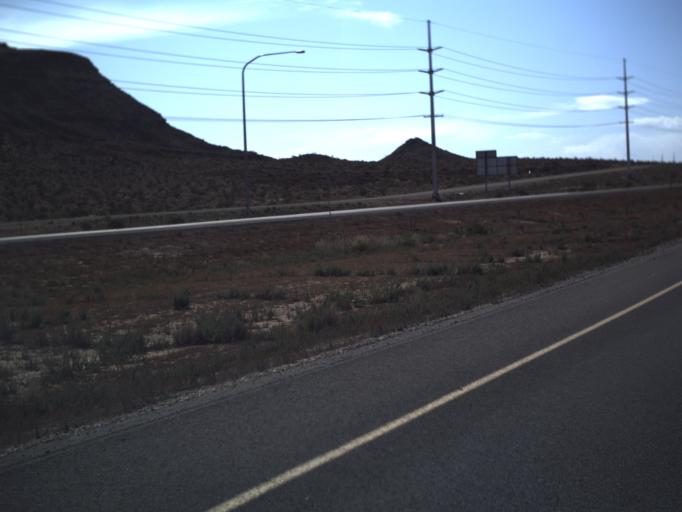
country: US
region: Utah
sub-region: Washington County
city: Washington
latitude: 37.0562
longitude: -113.4862
